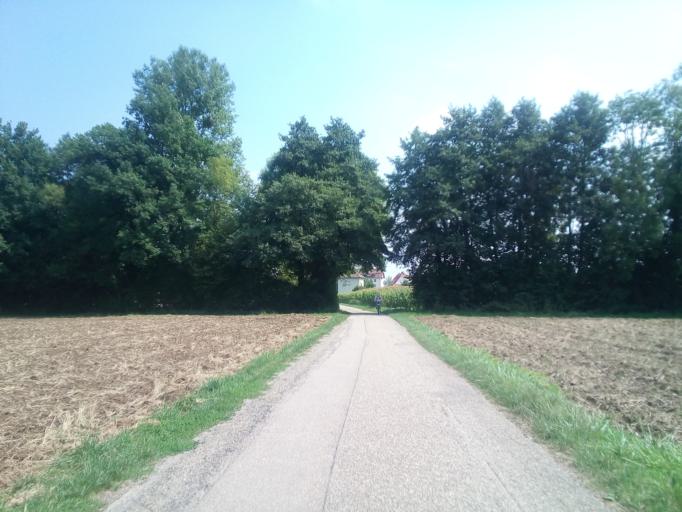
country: DE
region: Baden-Wuerttemberg
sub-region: Freiburg Region
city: Kehl
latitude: 48.6010
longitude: 7.8616
